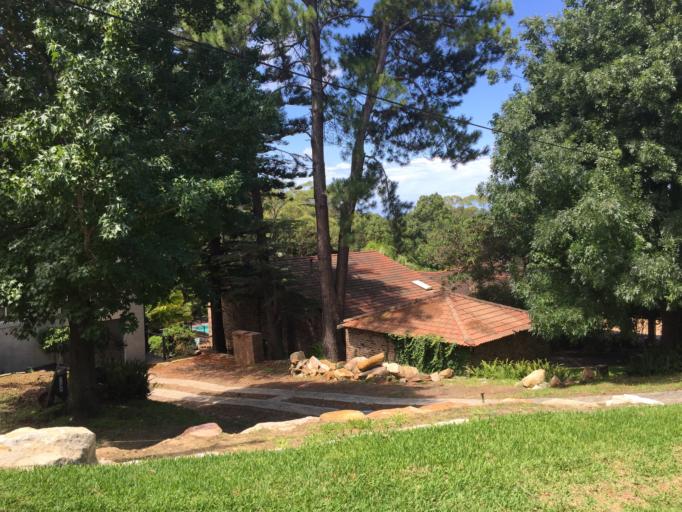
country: AU
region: New South Wales
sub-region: Pittwater
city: North Narrabeen
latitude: -33.7053
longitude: 151.2831
